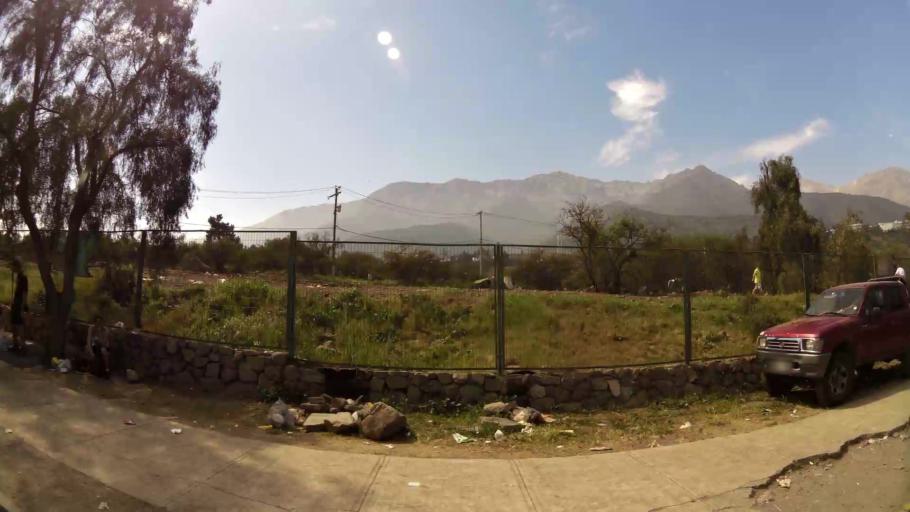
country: CL
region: Santiago Metropolitan
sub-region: Provincia de Santiago
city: Villa Presidente Frei, Nunoa, Santiago, Chile
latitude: -33.4813
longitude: -70.5234
